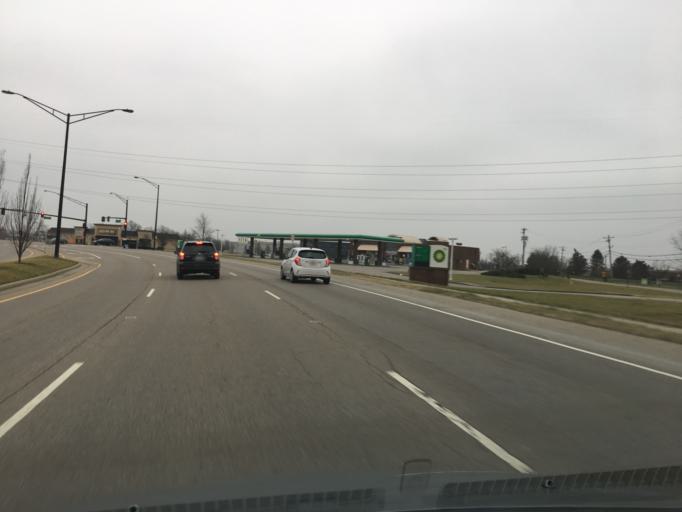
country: US
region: Ohio
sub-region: Butler County
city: Beckett Ridge
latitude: 39.3262
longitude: -84.4352
